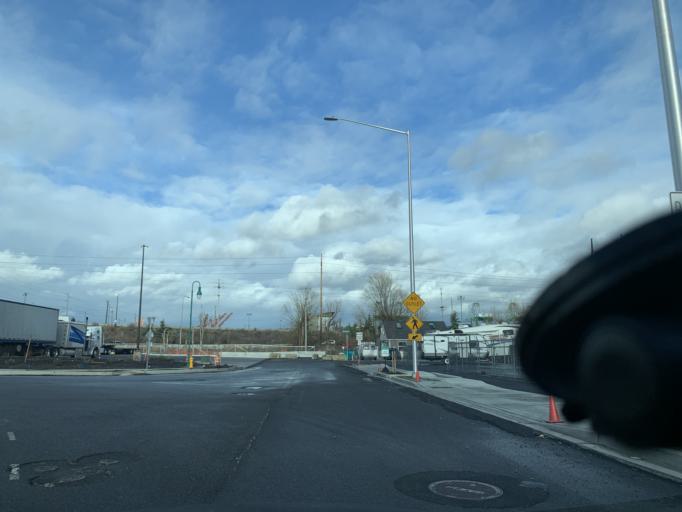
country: US
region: Washington
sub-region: Pierce County
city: Fife
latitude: 47.2459
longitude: -122.3835
